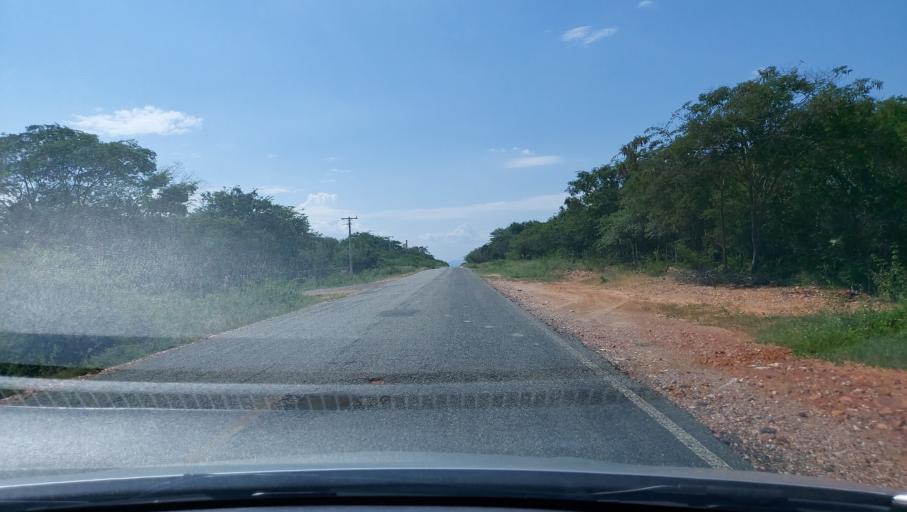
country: BR
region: Bahia
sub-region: Oliveira Dos Brejinhos
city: Beira Rio
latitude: -12.1770
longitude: -42.5434
